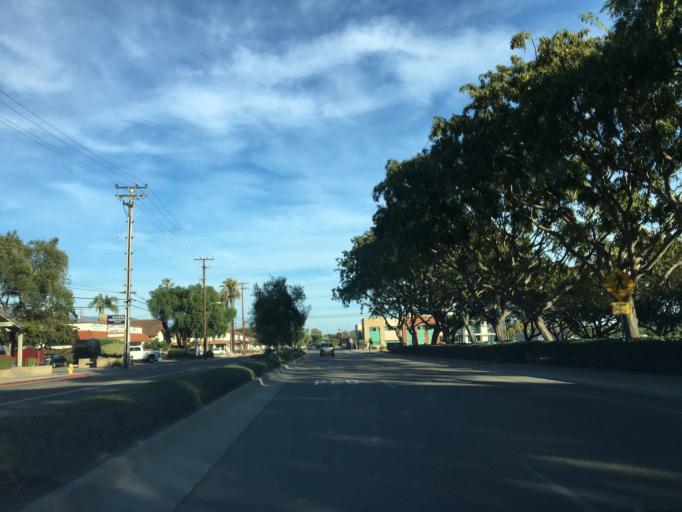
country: US
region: California
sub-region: Santa Barbara County
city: Goleta
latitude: 34.4351
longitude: -119.8124
